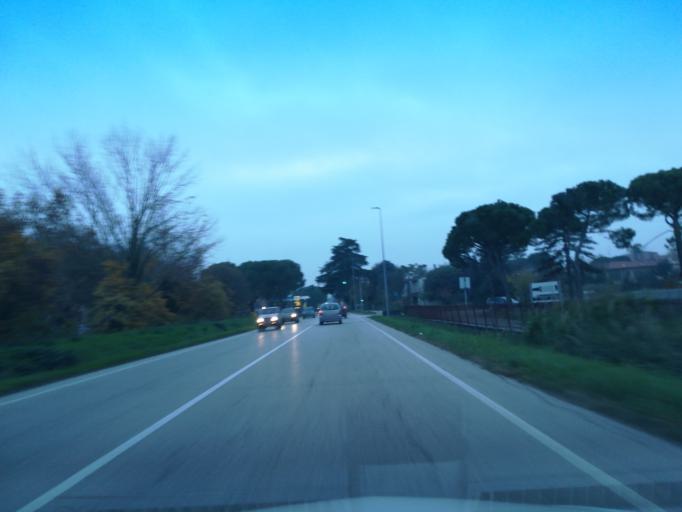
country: IT
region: Emilia-Romagna
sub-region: Provincia di Ravenna
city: Faenza
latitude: 44.2988
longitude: 11.8901
